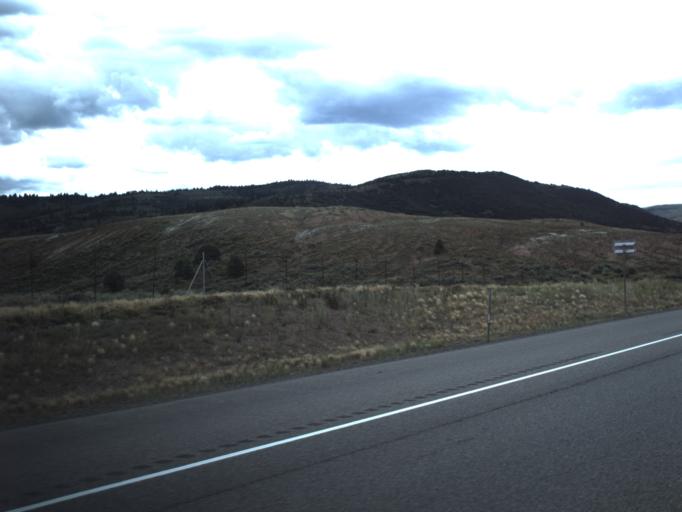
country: US
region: Utah
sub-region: Carbon County
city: Helper
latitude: 39.9224
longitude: -111.0674
